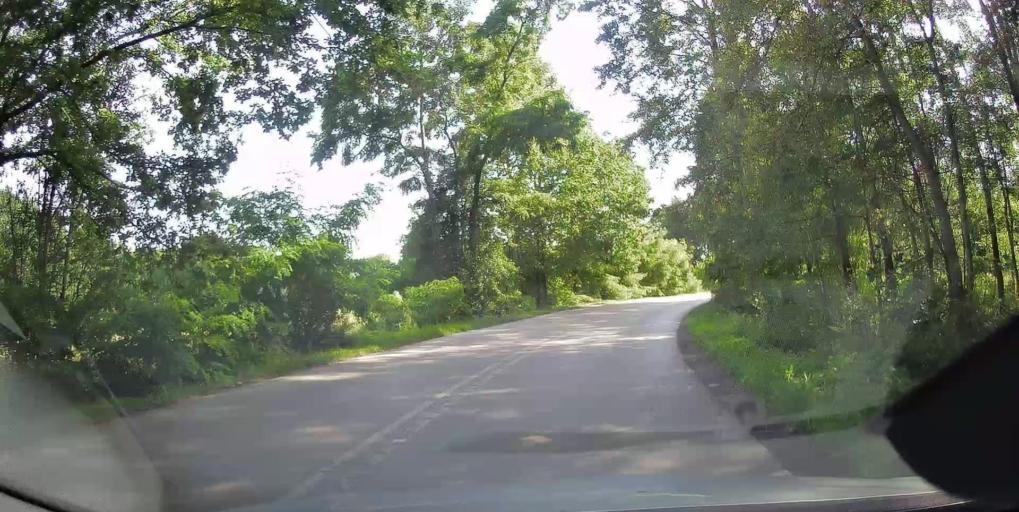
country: PL
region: Lodz Voivodeship
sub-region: Powiat opoczynski
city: Mniszkow
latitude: 51.3385
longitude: 20.0388
